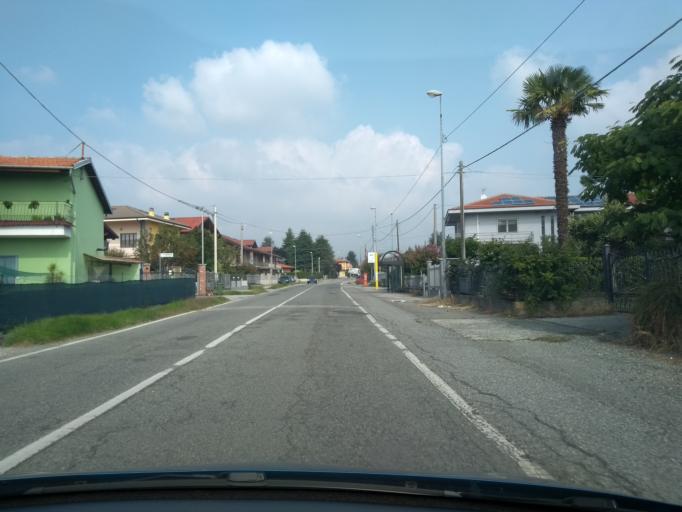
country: IT
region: Piedmont
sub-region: Provincia di Torino
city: Oglianico
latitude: 45.3535
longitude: 7.6922
